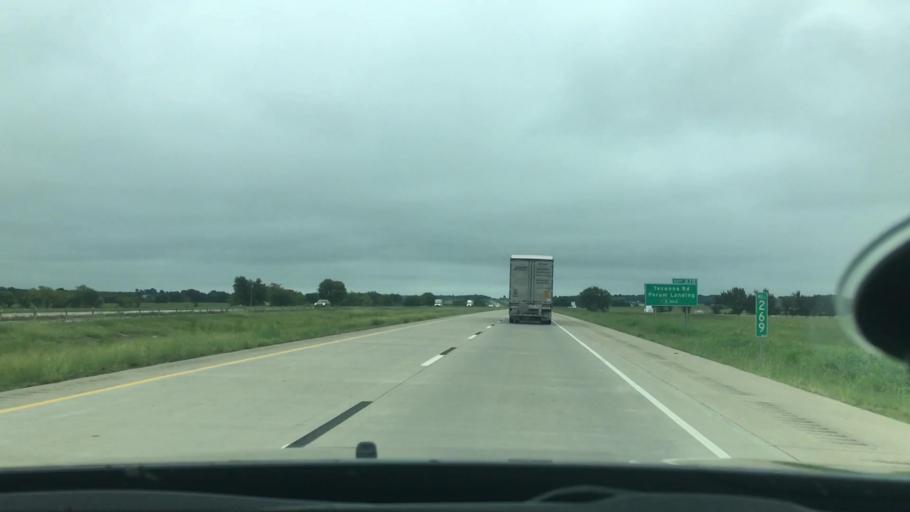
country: US
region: Oklahoma
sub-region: McIntosh County
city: Checotah
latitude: 35.4564
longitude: -95.4733
